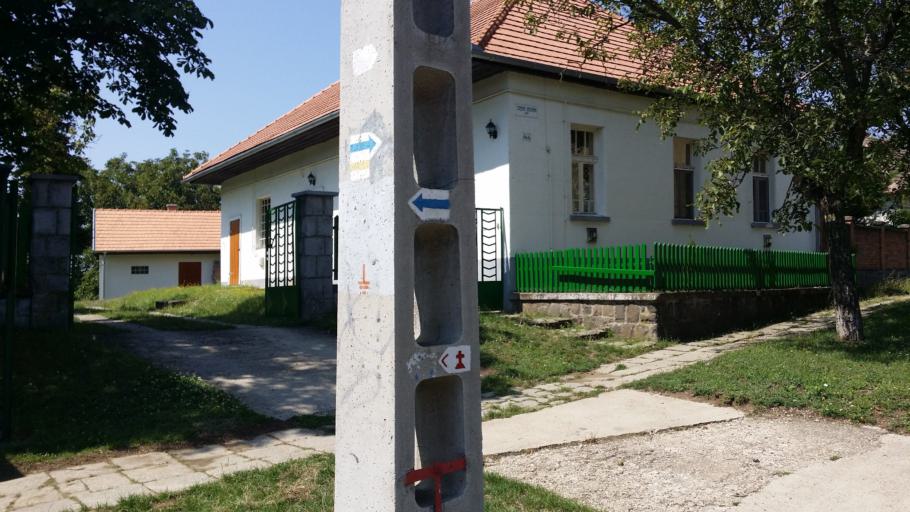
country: HU
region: Pest
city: Kismaros
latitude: 47.8780
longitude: 18.9324
